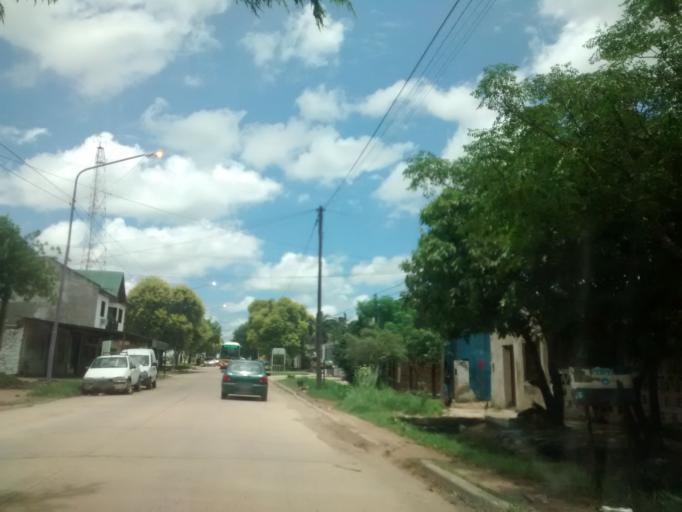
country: AR
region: Chaco
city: Fontana
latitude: -27.4345
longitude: -59.0018
